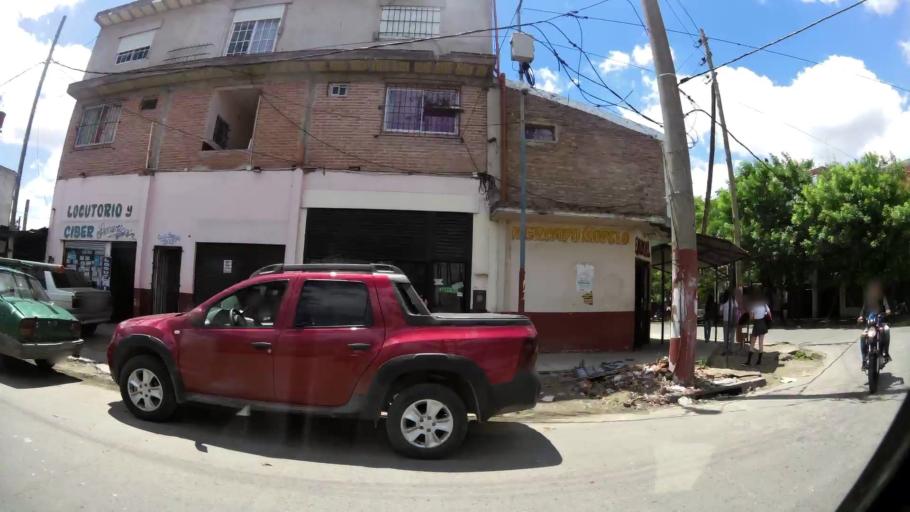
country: AR
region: Buenos Aires F.D.
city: Villa Lugano
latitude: -34.6972
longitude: -58.4406
